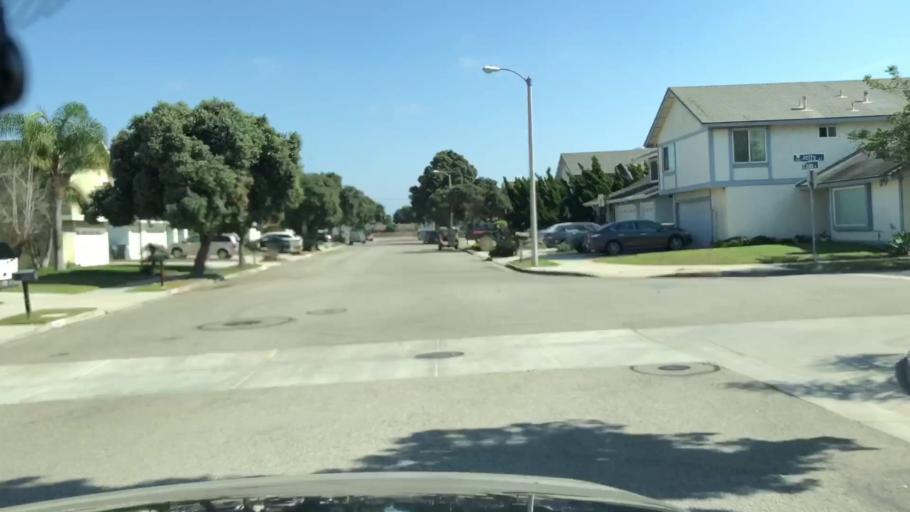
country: US
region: California
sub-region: Ventura County
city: Channel Islands Beach
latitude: 34.1832
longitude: -119.2110
